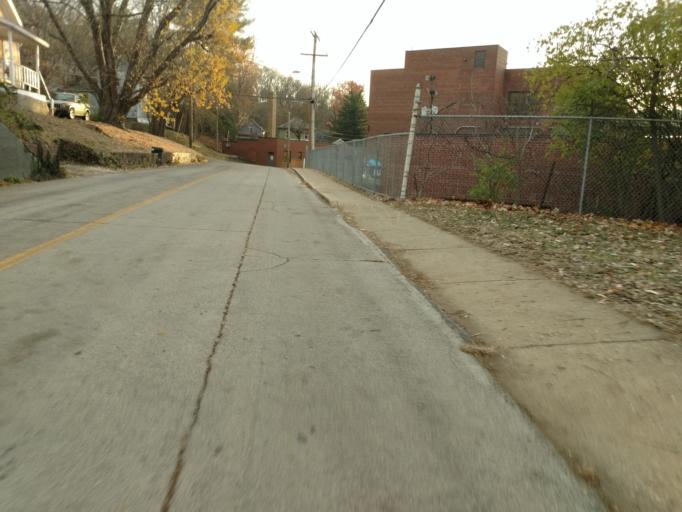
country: US
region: Ohio
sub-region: Athens County
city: Athens
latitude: 39.3309
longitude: -82.1088
